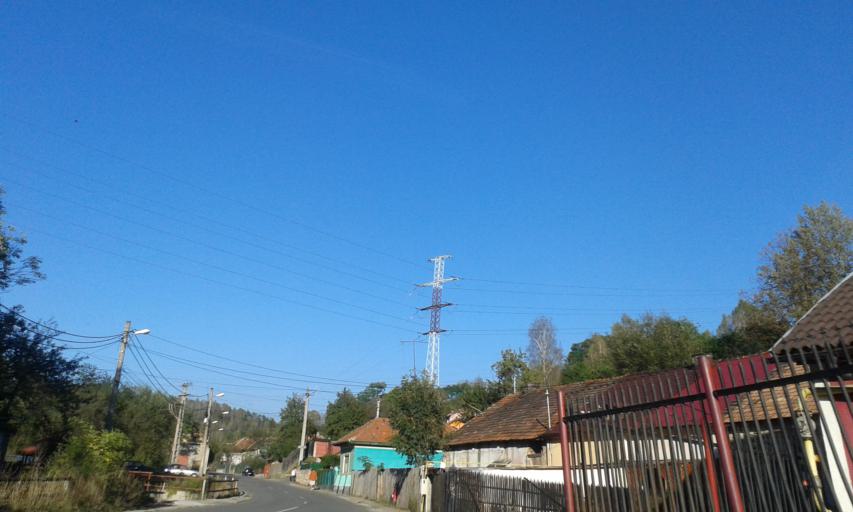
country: RO
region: Hunedoara
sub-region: Municipiul Petrosani
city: Petrosani
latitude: 45.4230
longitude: 23.3758
